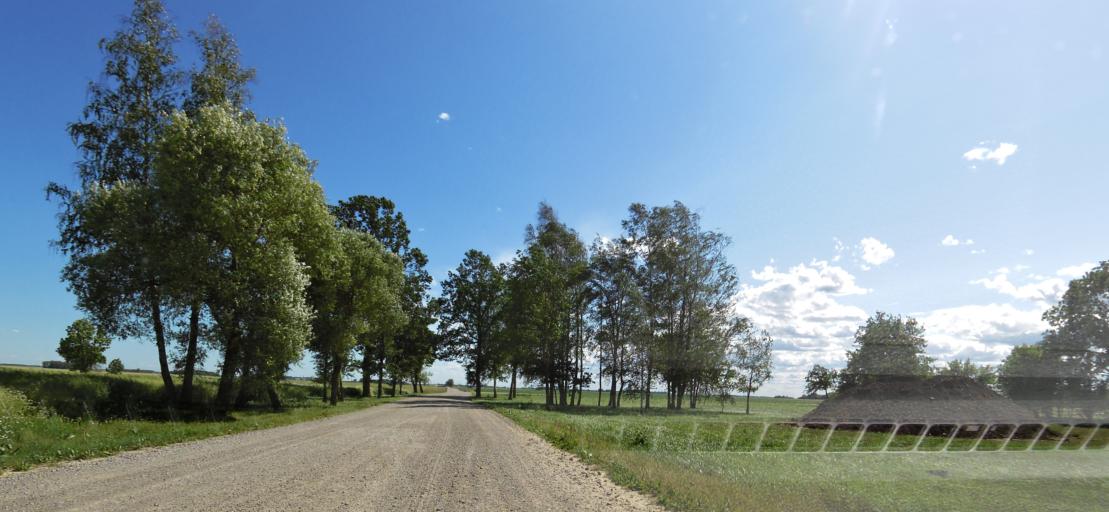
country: LV
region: Bauskas Rajons
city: Bauska
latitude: 56.2127
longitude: 24.2073
